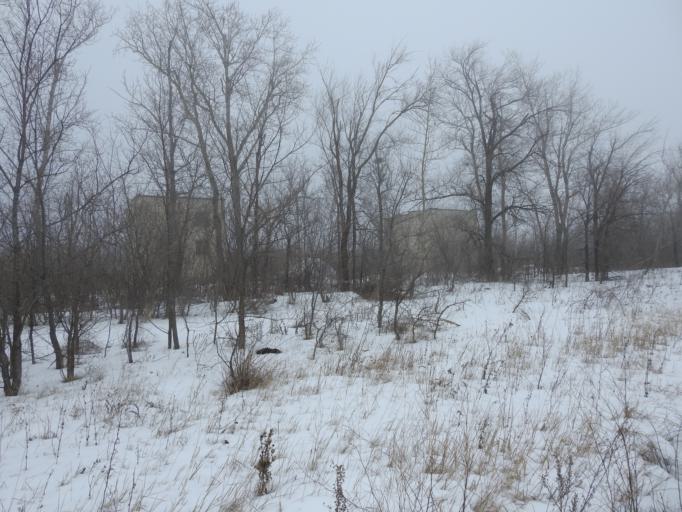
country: RU
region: Saratov
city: Sokolovyy
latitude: 51.4981
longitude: 45.8120
